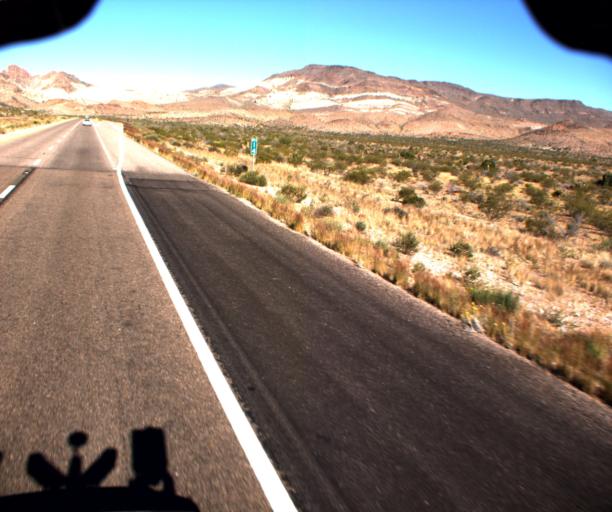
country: US
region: Arizona
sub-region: Mohave County
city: Golden Valley
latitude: 35.2289
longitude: -114.3569
